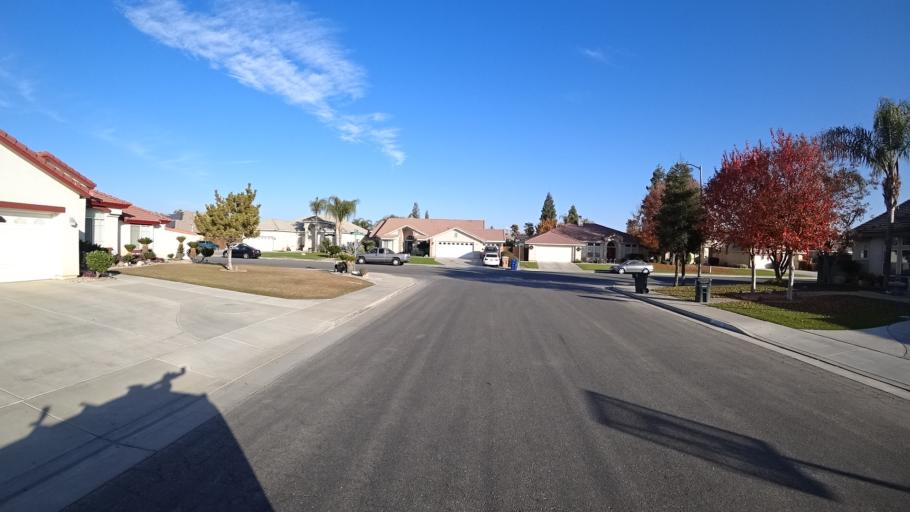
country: US
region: California
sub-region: Kern County
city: Greenfield
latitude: 35.2754
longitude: -119.0496
